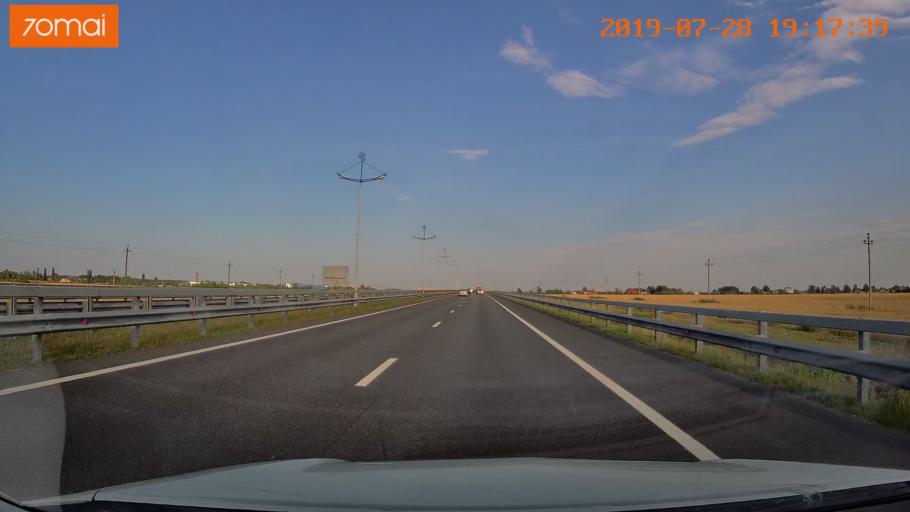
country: RU
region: Kaliningrad
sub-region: Zelenogradskiy Rayon
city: Zelenogradsk
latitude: 54.9210
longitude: 20.4087
